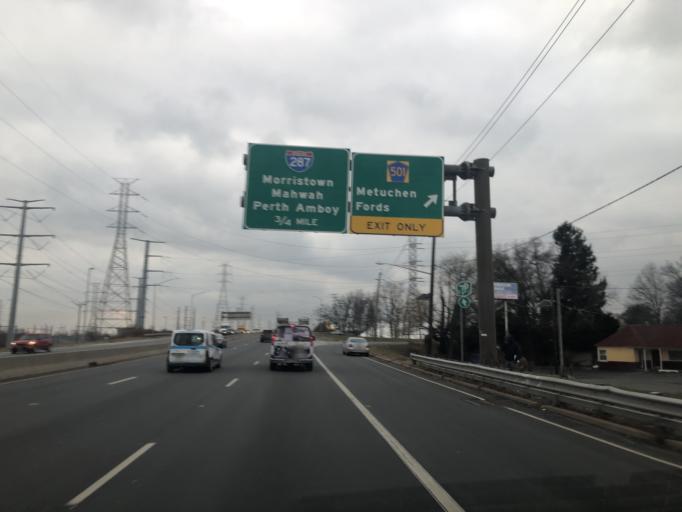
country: US
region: New Jersey
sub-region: Middlesex County
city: Metuchen
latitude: 40.5374
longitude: -74.3422
